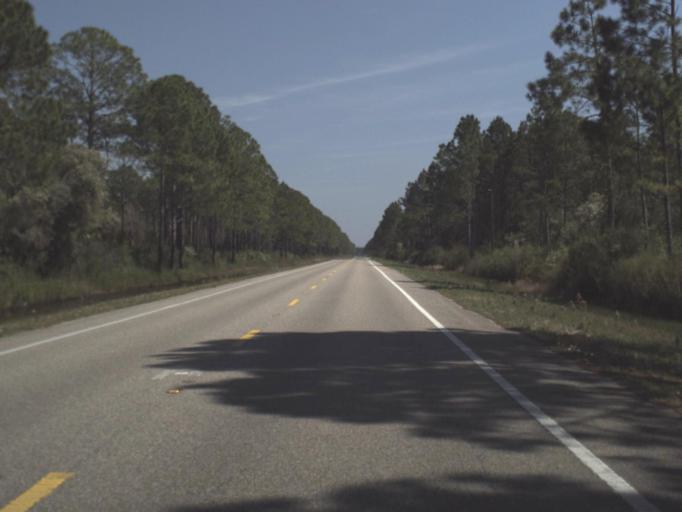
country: US
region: Florida
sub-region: Franklin County
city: Apalachicola
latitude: 29.7292
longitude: -85.1356
